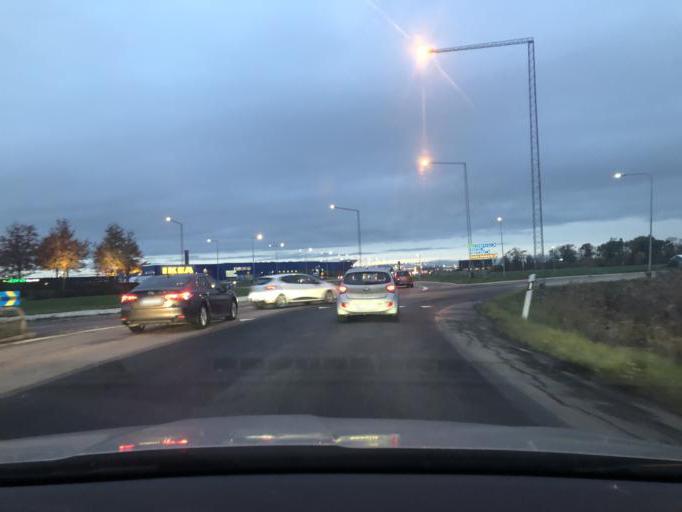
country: SE
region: Uppsala
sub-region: Uppsala Kommun
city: Saevja
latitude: 59.8446
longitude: 17.7023
